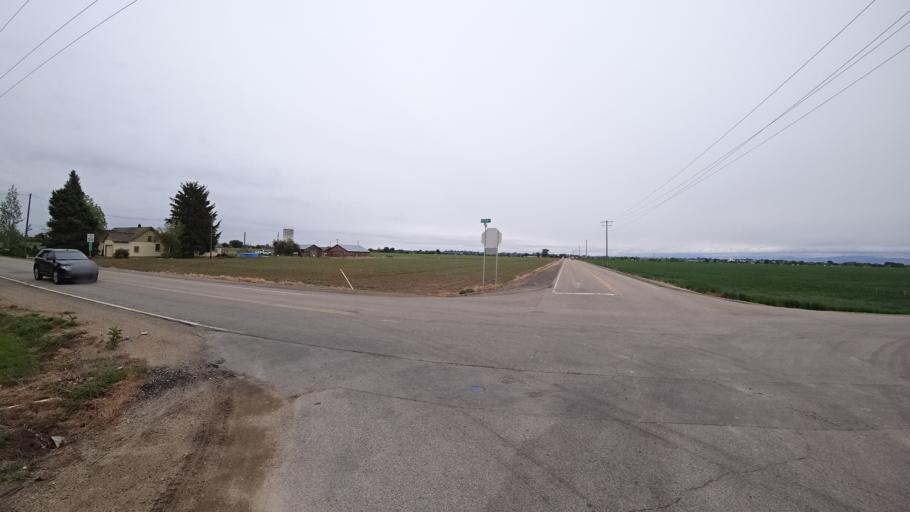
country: US
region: Idaho
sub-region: Ada County
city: Star
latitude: 43.6342
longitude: -116.4734
